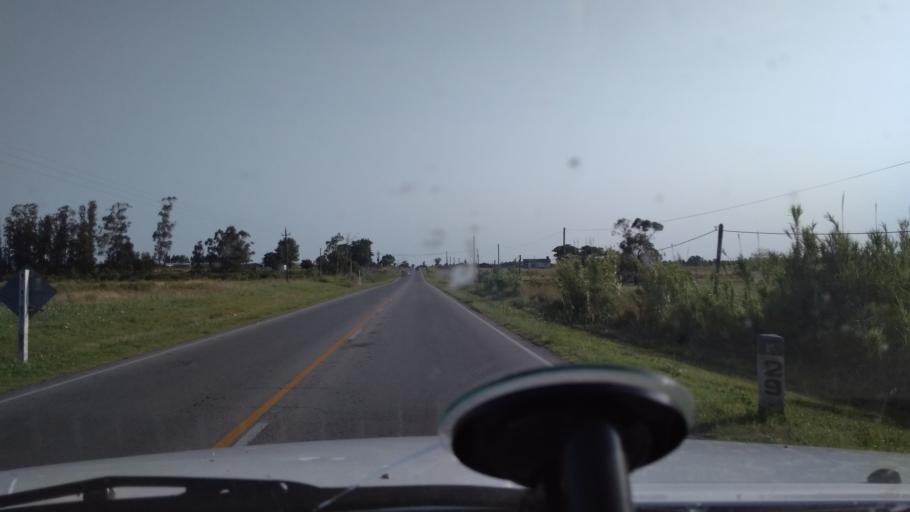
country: UY
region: Canelones
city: Joaquin Suarez
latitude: -34.6977
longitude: -56.0564
